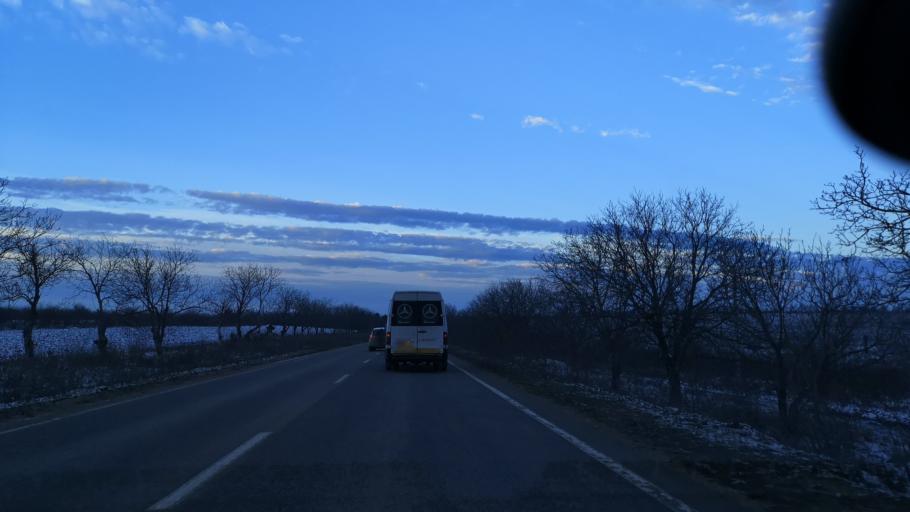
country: MD
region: Orhei
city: Orhei
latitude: 47.5440
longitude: 28.7928
